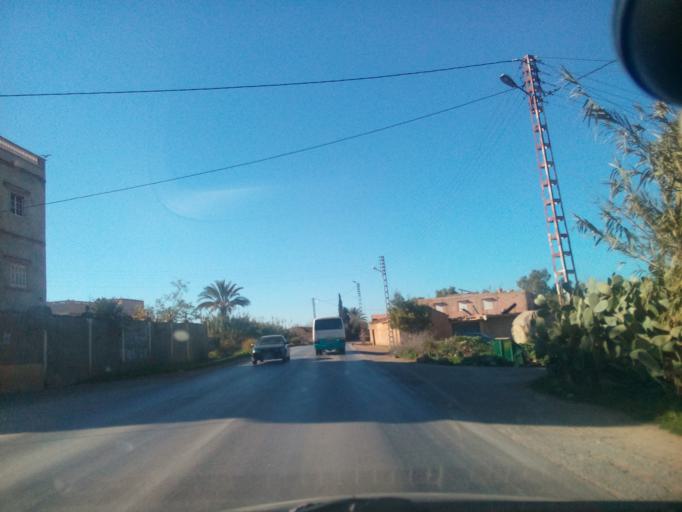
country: DZ
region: Relizane
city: Djidiouia
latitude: 35.8933
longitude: 0.7238
